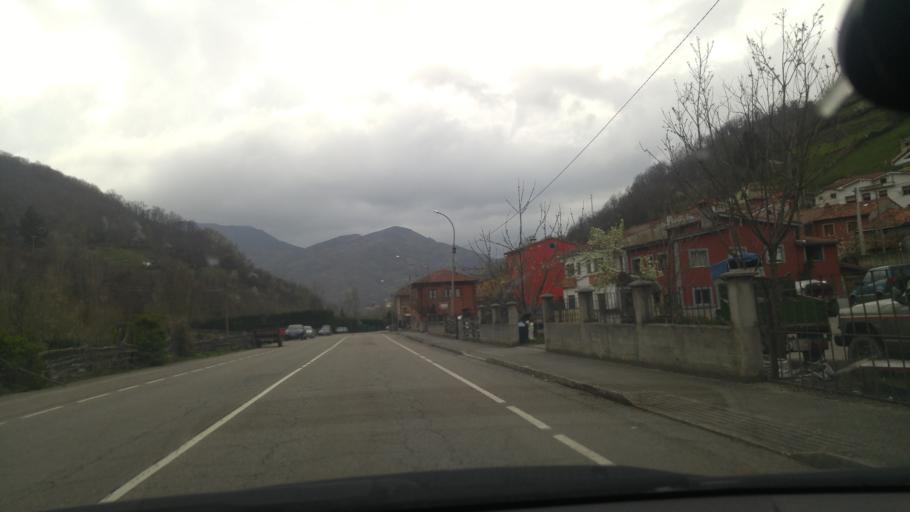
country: ES
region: Asturias
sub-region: Province of Asturias
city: Rio Aller
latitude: 43.1184
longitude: -5.5407
